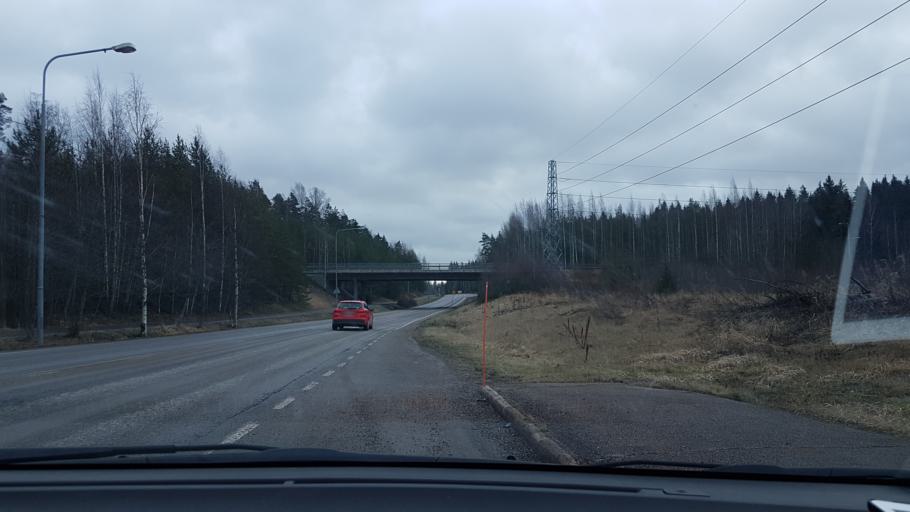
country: FI
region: Uusimaa
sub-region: Helsinki
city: Tuusula
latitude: 60.3781
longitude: 25.0521
